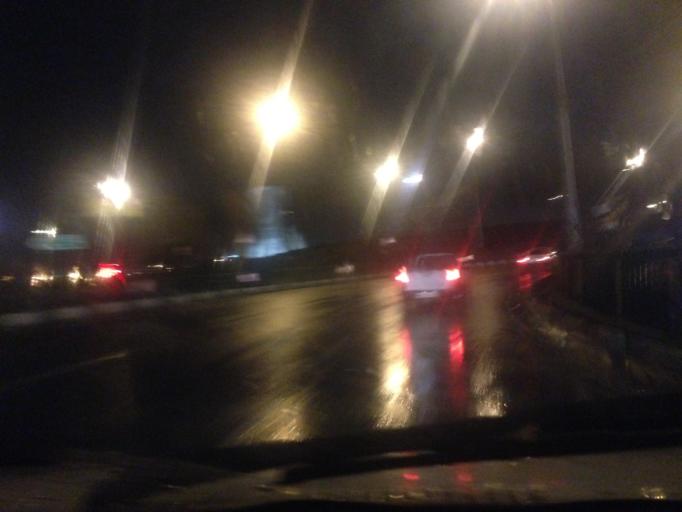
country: IR
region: Tehran
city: Tehran
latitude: 35.6967
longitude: 51.3389
